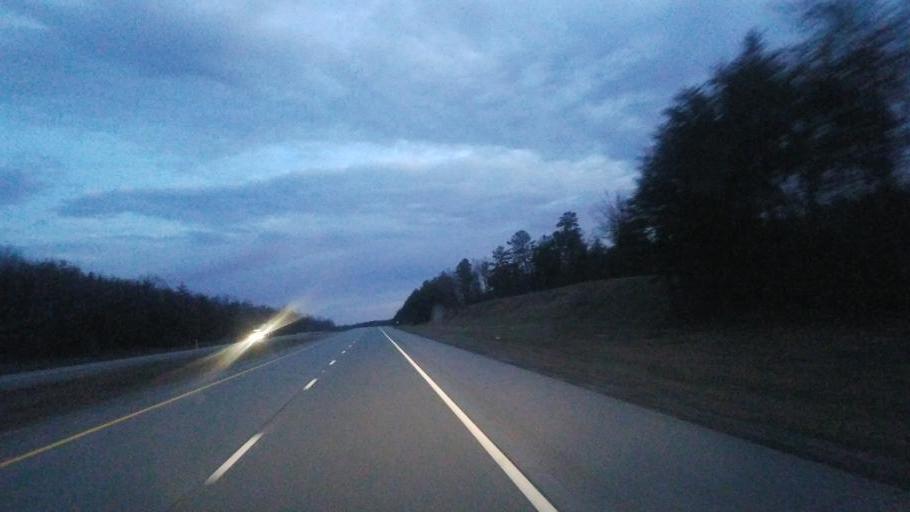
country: US
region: Tennessee
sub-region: Van Buren County
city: Spencer
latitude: 35.5889
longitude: -85.4706
